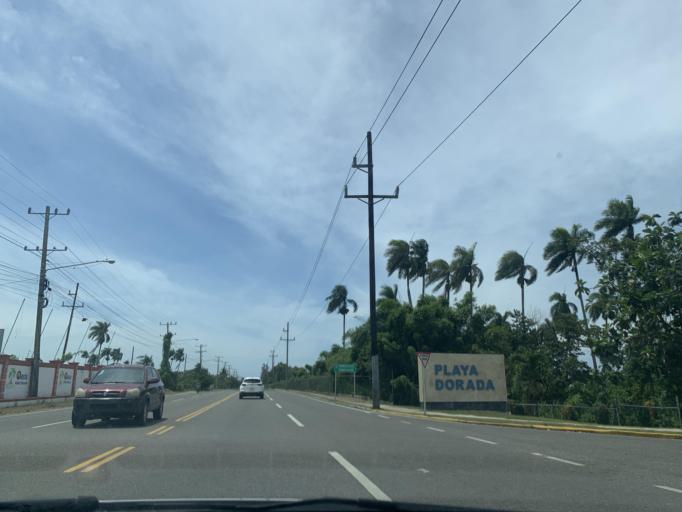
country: DO
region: Puerto Plata
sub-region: Puerto Plata
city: Puerto Plata
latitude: 19.7565
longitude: -70.6440
